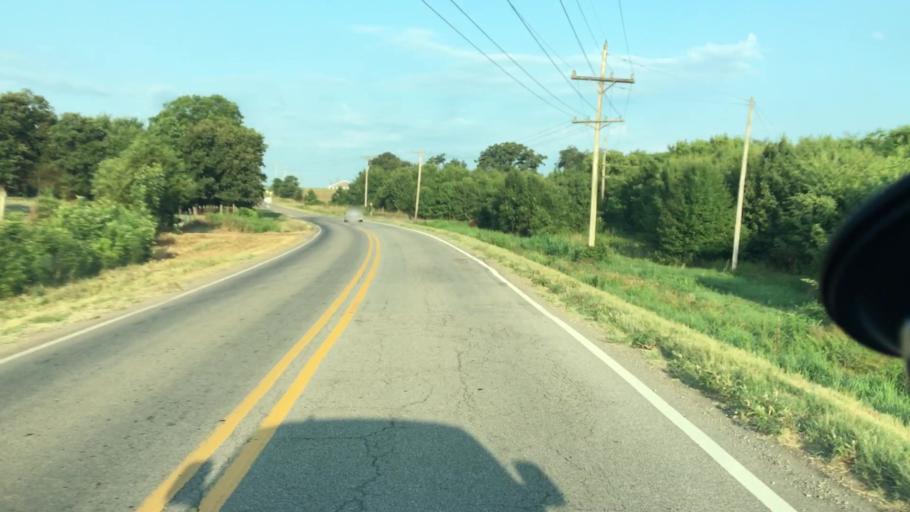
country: US
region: Arkansas
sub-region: Johnson County
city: Coal Hill
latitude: 35.3745
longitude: -93.5681
